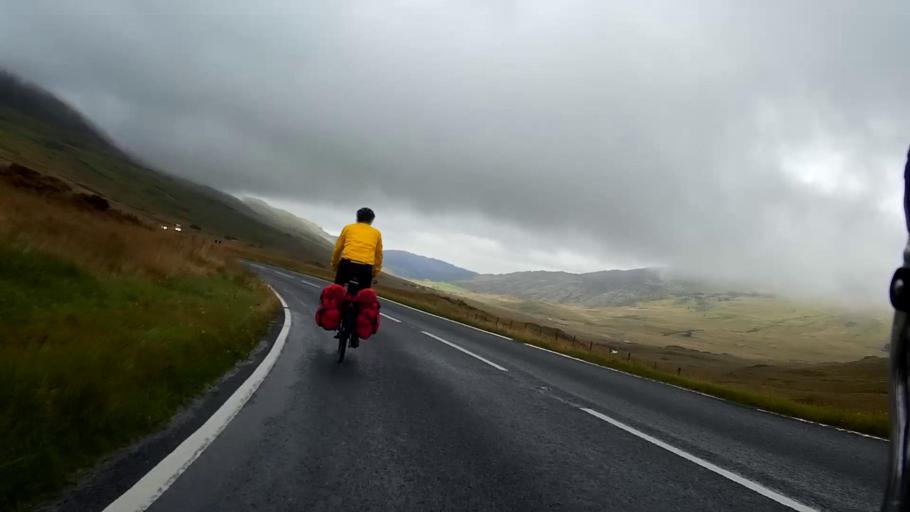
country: GB
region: Wales
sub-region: Gwynedd
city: Blaenau-Ffestiniog
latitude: 53.0849
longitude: -3.9918
